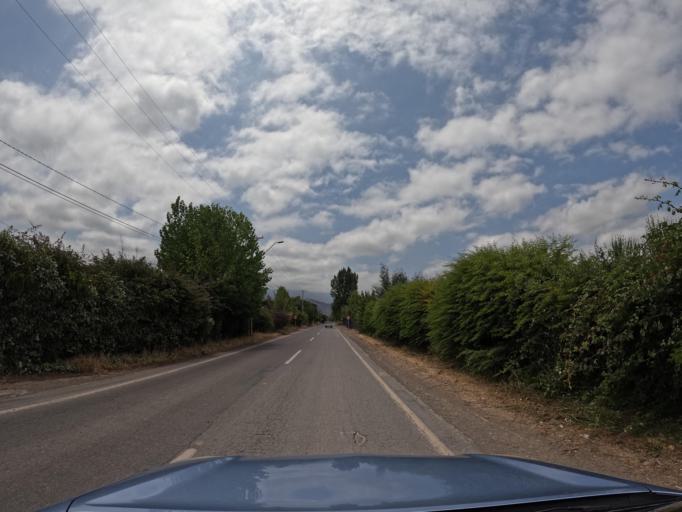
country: CL
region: O'Higgins
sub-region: Provincia de Colchagua
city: Chimbarongo
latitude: -34.7445
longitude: -70.9664
